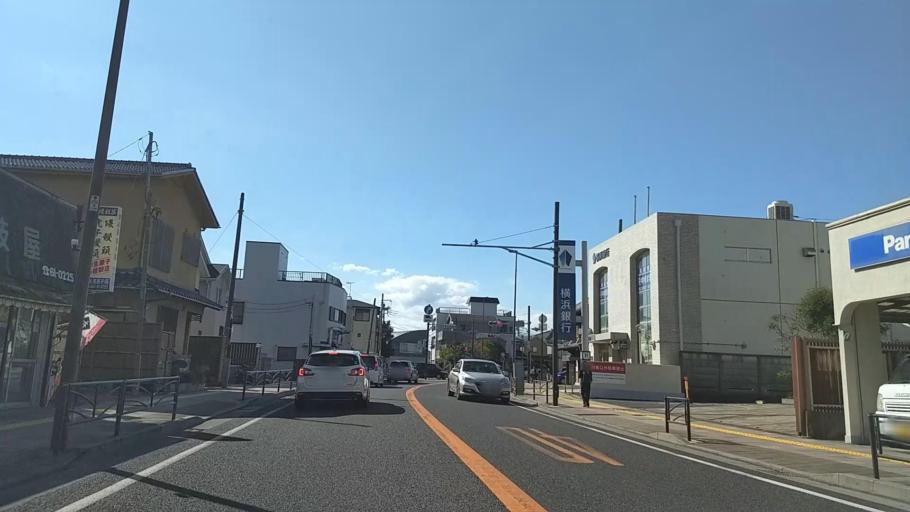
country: JP
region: Kanagawa
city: Oiso
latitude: 35.3079
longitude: 139.3145
